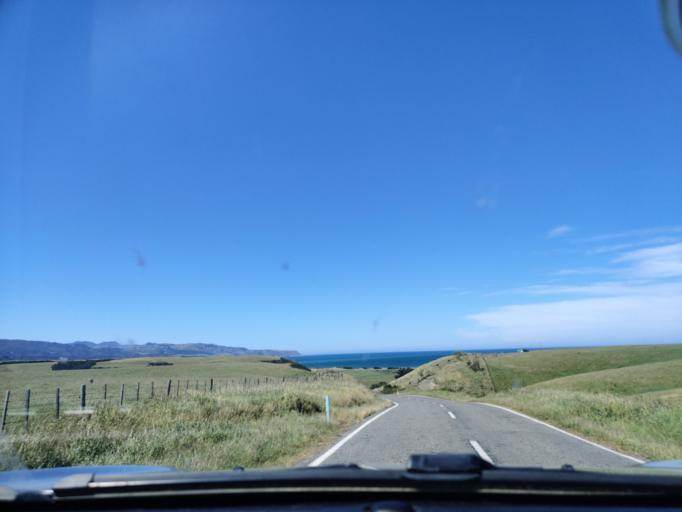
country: NZ
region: Wellington
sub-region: Upper Hutt City
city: Upper Hutt
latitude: -41.3970
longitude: 175.1767
